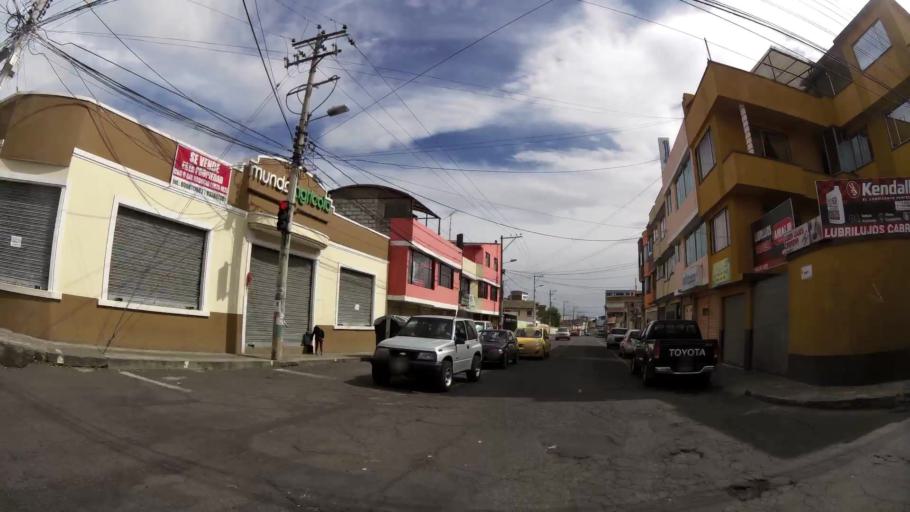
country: EC
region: Cotopaxi
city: Latacunga
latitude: -0.9281
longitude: -78.6127
